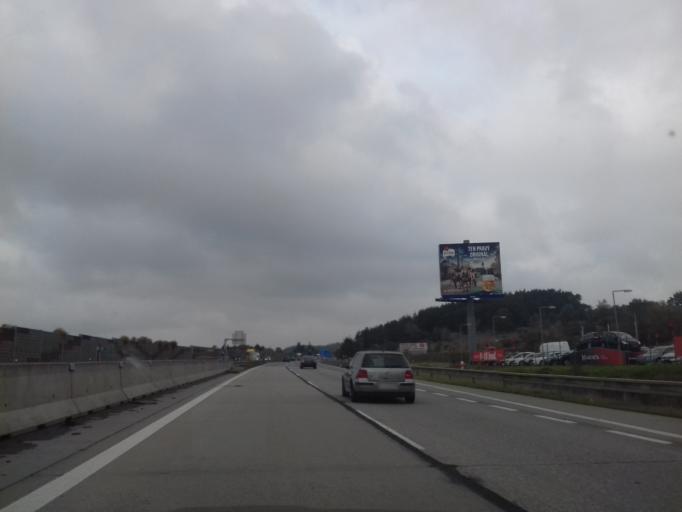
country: CZ
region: Vysocina
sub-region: Okres Zd'ar nad Sazavou
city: Velke Mezirici
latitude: 49.3464
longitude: 16.0424
